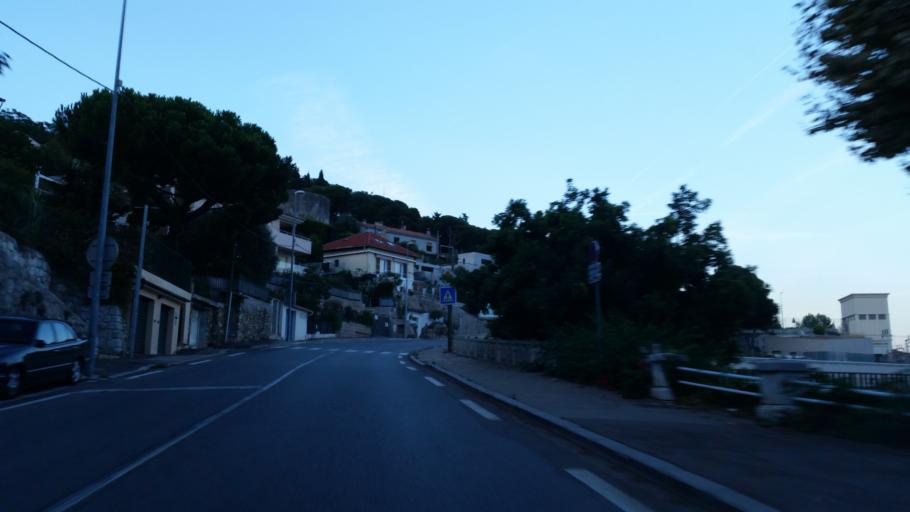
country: MC
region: Commune de Monaco
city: Moneghetti
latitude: 43.7419
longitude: 7.4162
